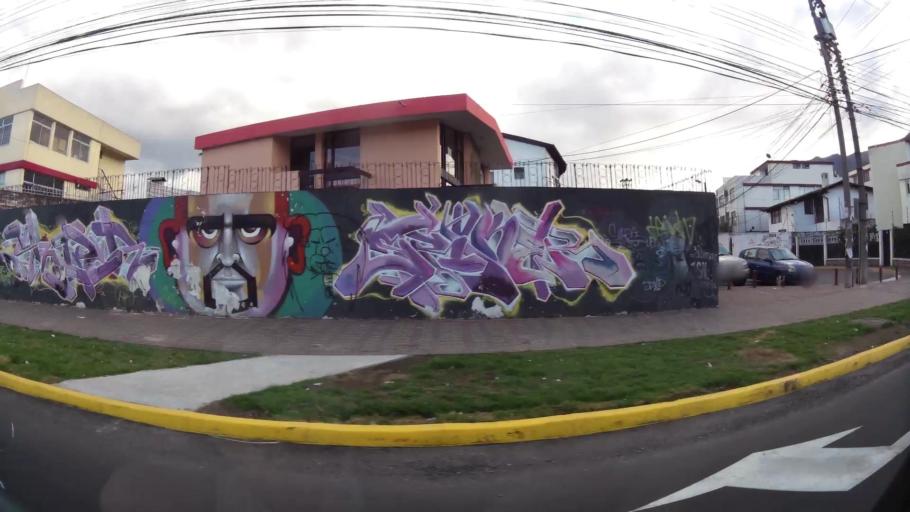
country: EC
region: Pichincha
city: Quito
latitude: -0.1657
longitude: -78.4842
